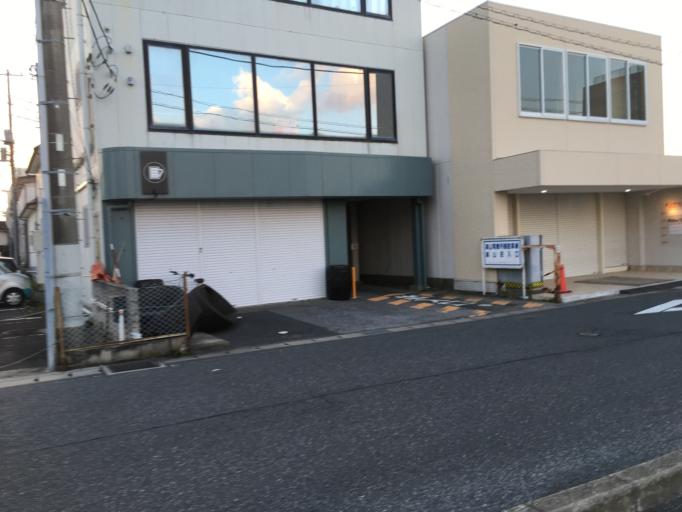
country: JP
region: Chiba
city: Tateyama
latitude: 34.9953
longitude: 139.8624
